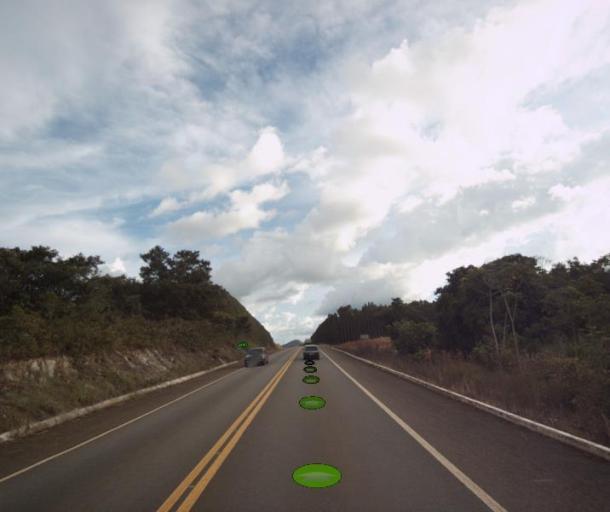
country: BR
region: Goias
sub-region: Niquelandia
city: Niquelandia
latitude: -14.5609
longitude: -48.5576
